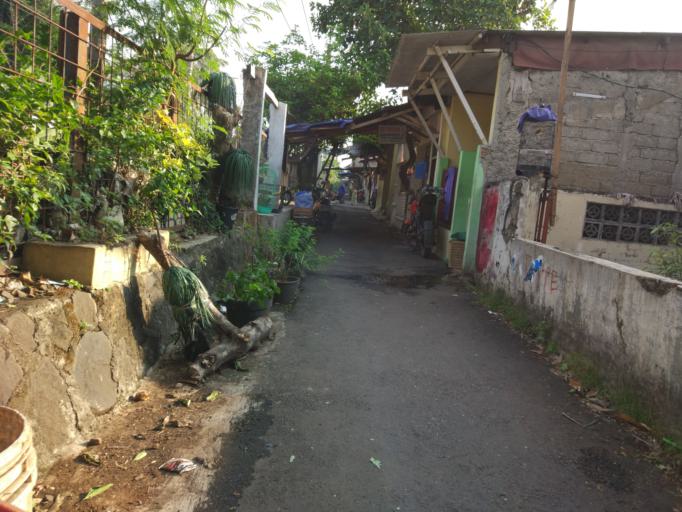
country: ID
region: Jakarta Raya
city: Jakarta
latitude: -6.2400
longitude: 106.8587
